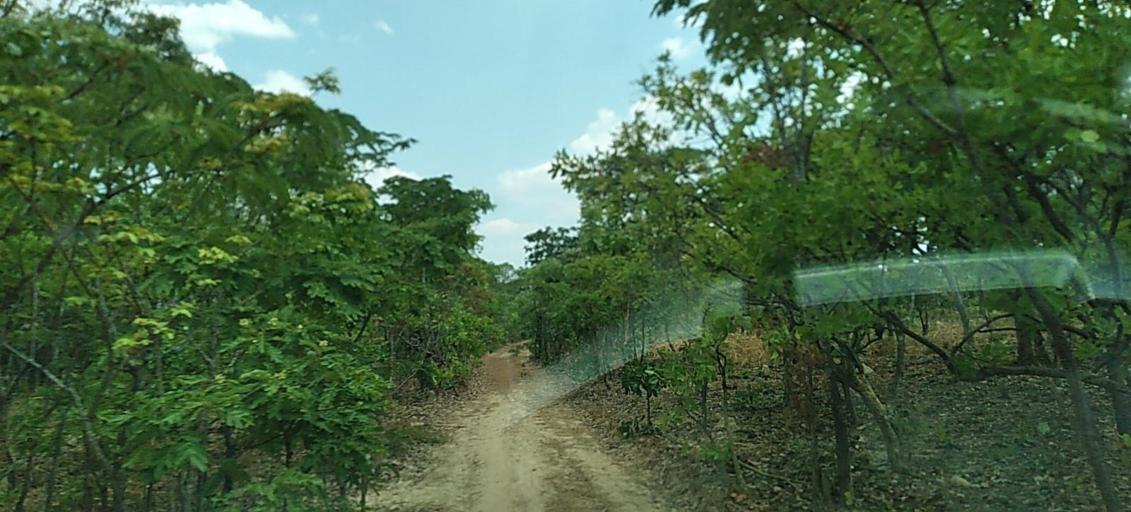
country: CD
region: Katanga
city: Kipushi
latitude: -11.9795
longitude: 27.4153
